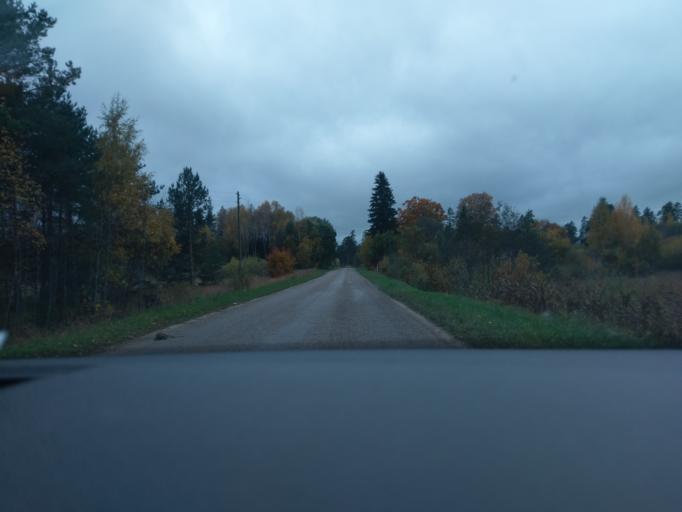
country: LV
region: Talsu Rajons
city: Stende
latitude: 57.0811
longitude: 22.2778
